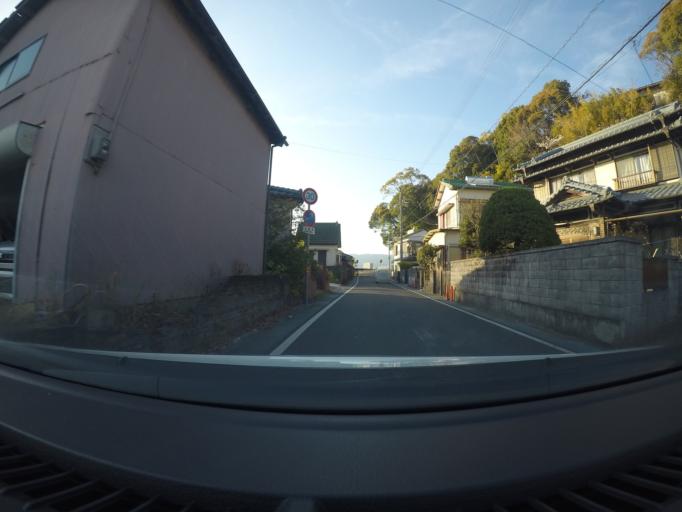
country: JP
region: Kochi
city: Kochi-shi
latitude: 33.5443
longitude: 133.5703
